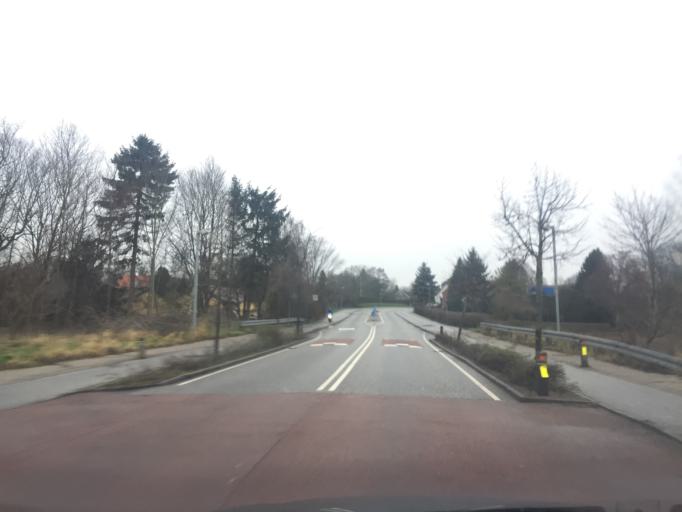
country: DK
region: Zealand
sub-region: Soro Kommune
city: Soro
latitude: 55.4492
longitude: 11.5575
